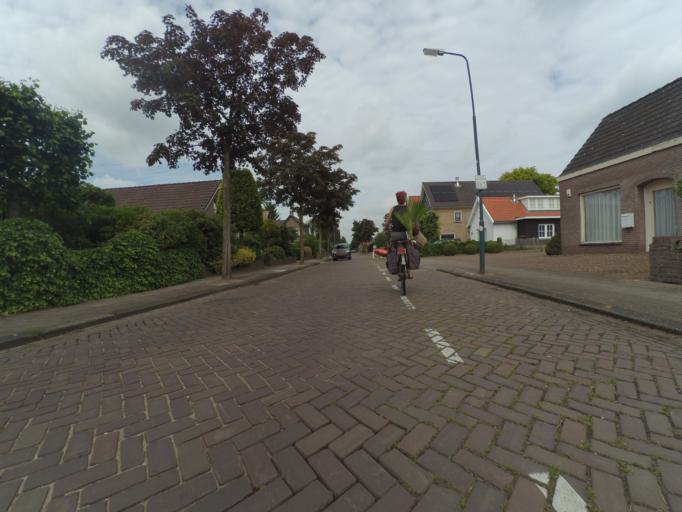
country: NL
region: Gelderland
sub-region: Gemeente Buren
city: Lienden
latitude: 51.9863
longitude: 5.5067
